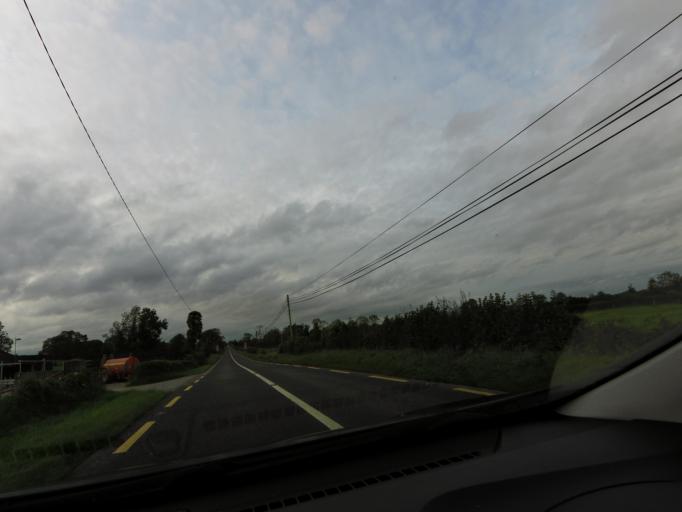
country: IE
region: Leinster
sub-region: Uibh Fhaili
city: Ferbane
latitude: 53.3679
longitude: -7.8555
